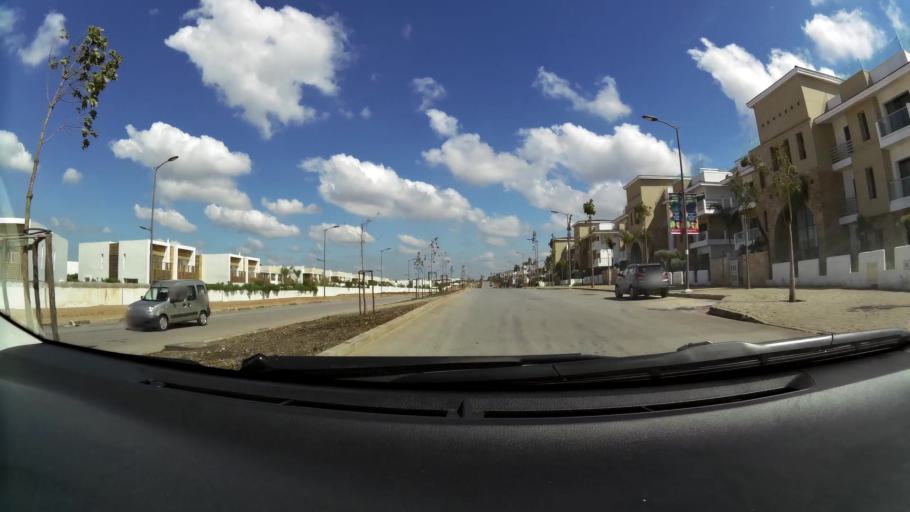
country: MA
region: Grand Casablanca
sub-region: Nouaceur
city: Bouskoura
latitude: 33.4861
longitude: -7.5995
